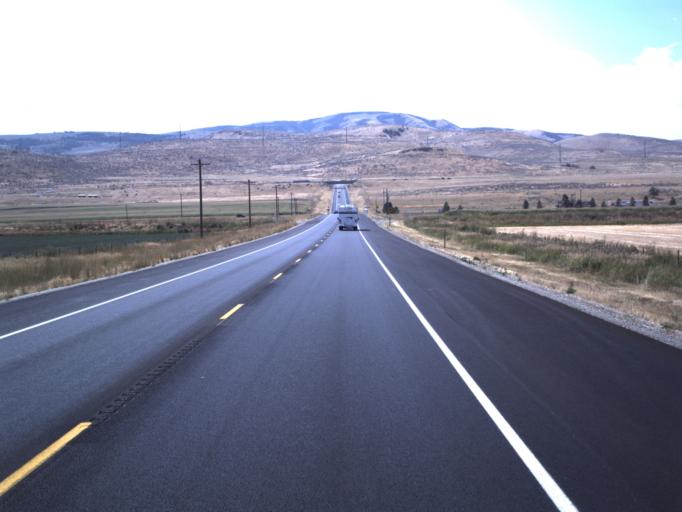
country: US
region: Utah
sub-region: Box Elder County
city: Garland
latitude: 41.7848
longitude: -112.1582
